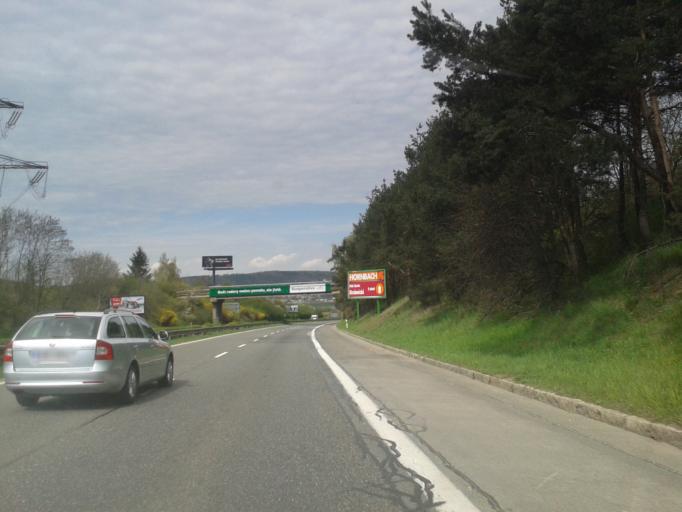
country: CZ
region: Central Bohemia
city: Vrane nad Vltavou
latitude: 49.9640
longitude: 14.3770
